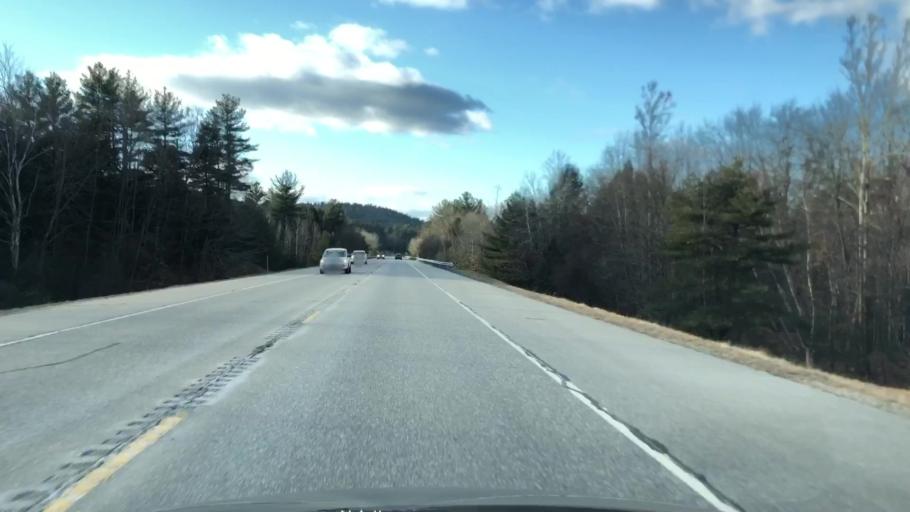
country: US
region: New Hampshire
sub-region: Hillsborough County
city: Milford
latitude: 42.8336
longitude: -71.6906
